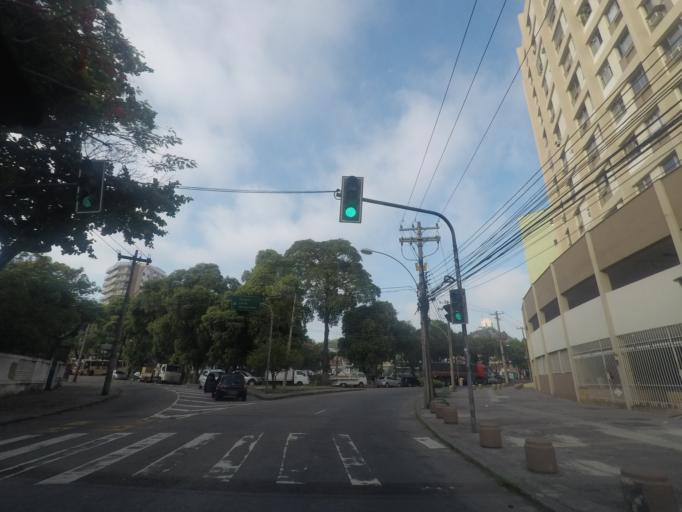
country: BR
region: Rio de Janeiro
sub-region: Duque De Caxias
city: Duque de Caxias
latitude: -22.8418
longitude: -43.2684
